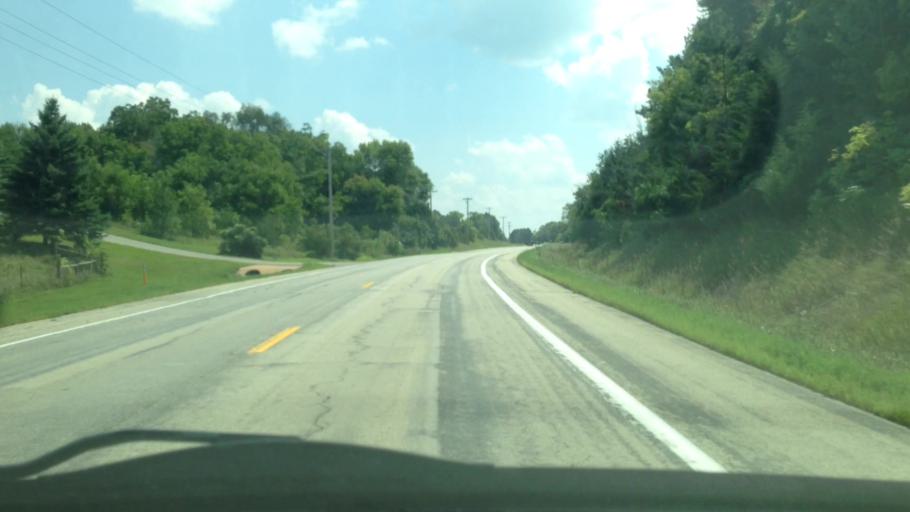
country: US
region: Minnesota
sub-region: Olmsted County
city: Rochester
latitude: 43.9655
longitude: -92.4324
